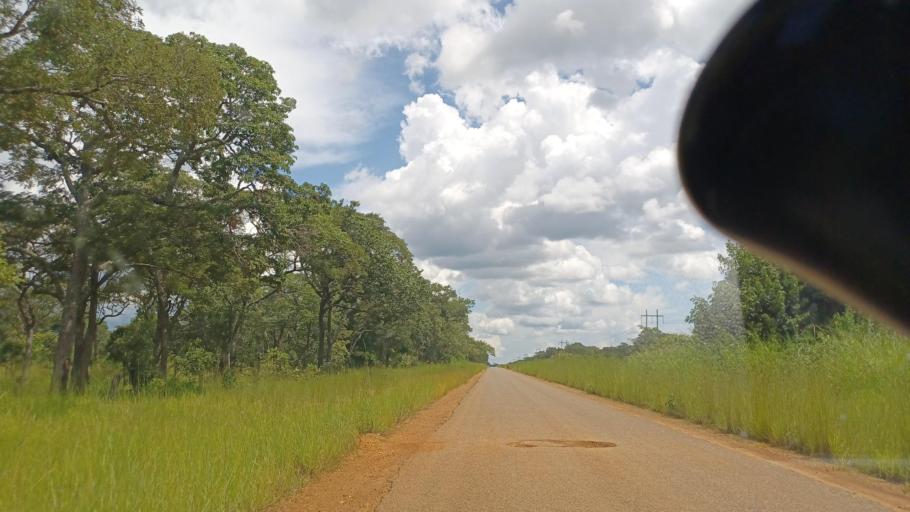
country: ZM
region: North-Western
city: Solwezi
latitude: -12.7049
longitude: 26.0319
